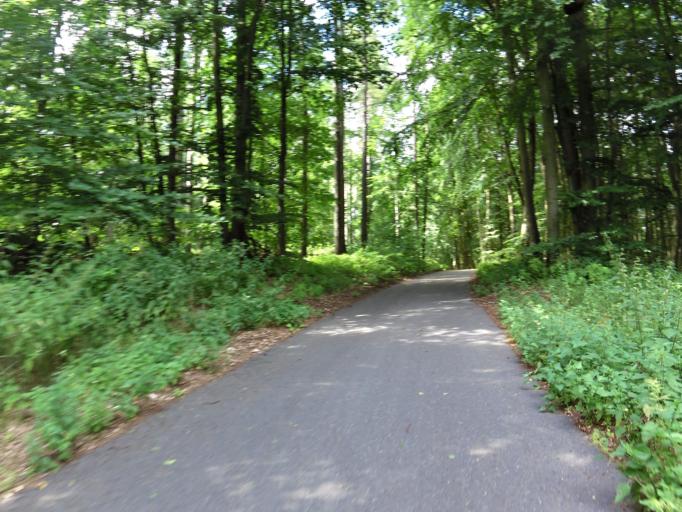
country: DE
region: Brandenburg
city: Lychen
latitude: 53.1901
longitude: 13.3390
